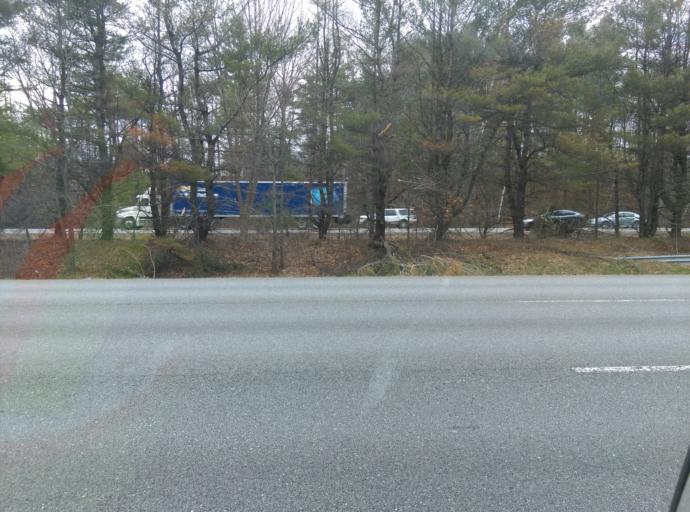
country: US
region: Massachusetts
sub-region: Essex County
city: Merrimac
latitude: 42.8327
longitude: -70.9813
